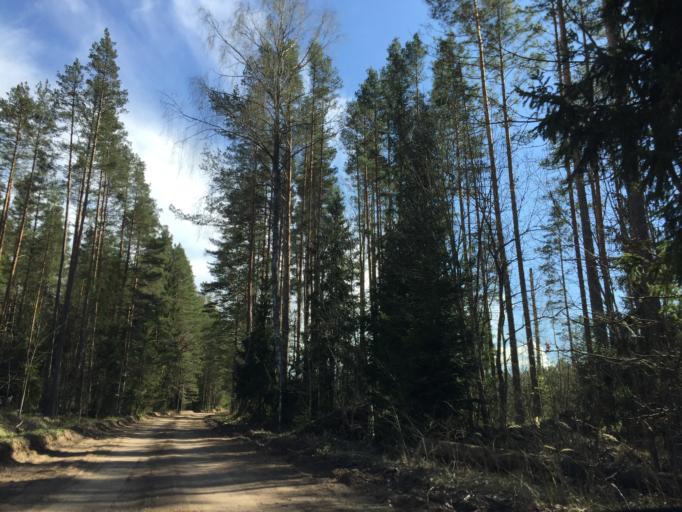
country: LV
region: Strenci
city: Strenci
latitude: 57.5724
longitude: 25.7097
